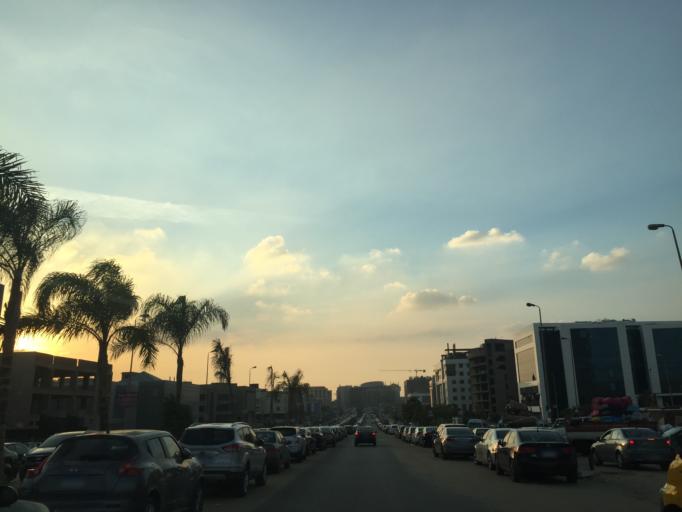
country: EG
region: Muhafazat al Qahirah
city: Cairo
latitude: 30.0199
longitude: 31.4243
